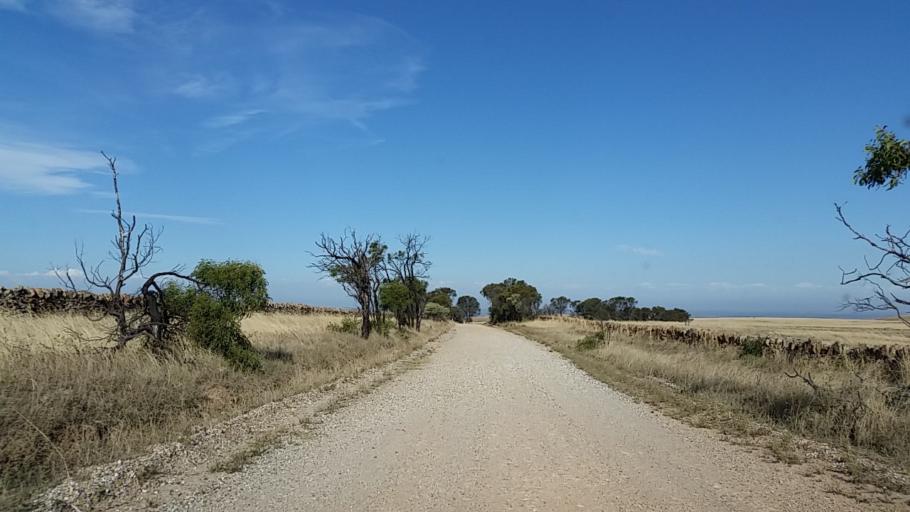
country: AU
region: South Australia
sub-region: Barossa
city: Angaston
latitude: -34.6142
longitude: 139.1976
